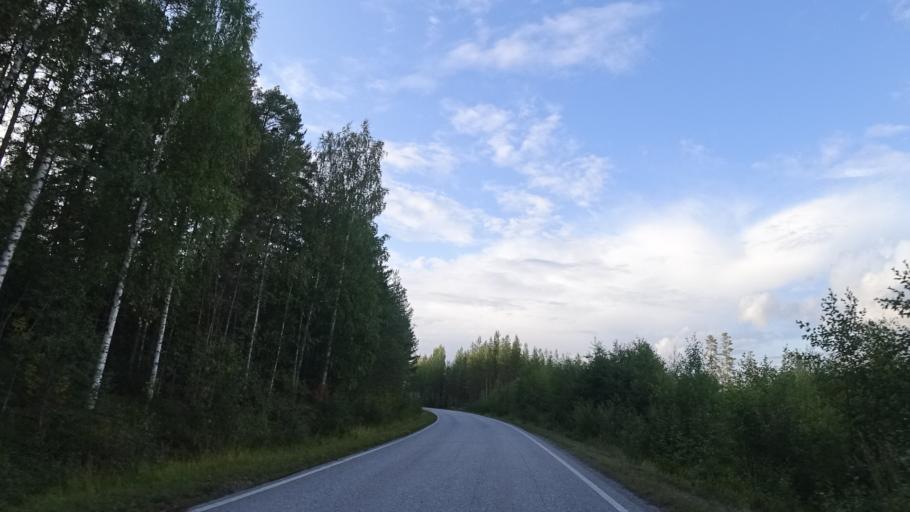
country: FI
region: North Karelia
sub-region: Pielisen Karjala
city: Lieksa
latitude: 63.3487
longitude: 30.2658
